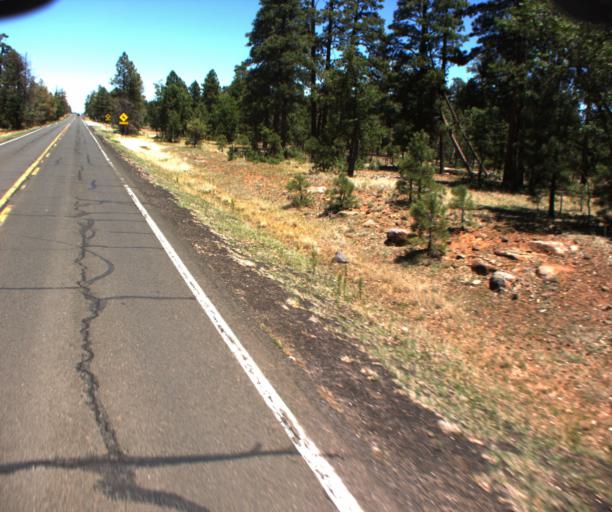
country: US
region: Arizona
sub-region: Gila County
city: Pine
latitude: 34.5838
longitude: -111.2584
